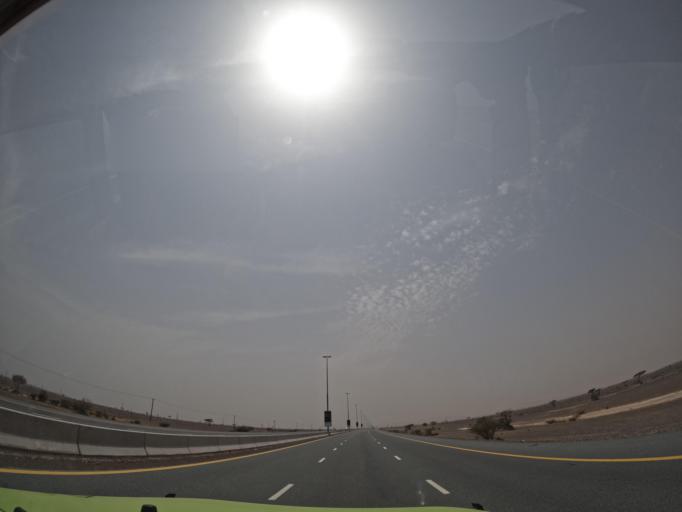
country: AE
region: Ash Shariqah
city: Adh Dhayd
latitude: 25.1429
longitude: 55.9920
